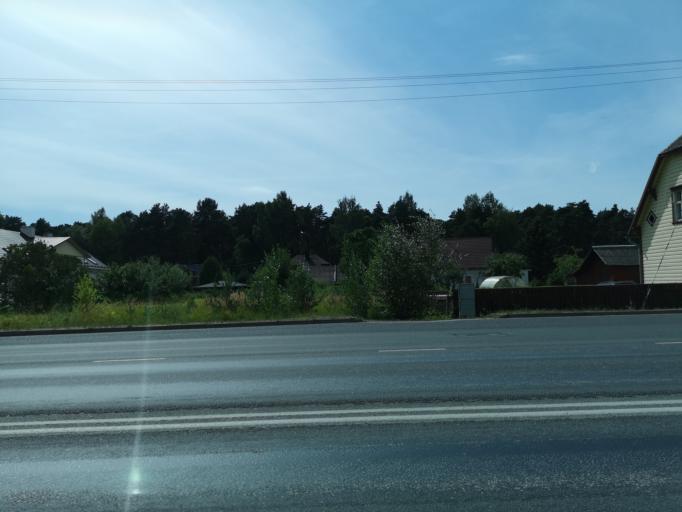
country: EE
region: Paernumaa
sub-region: Paernu linn
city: Parnu
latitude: 58.3650
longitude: 24.5574
